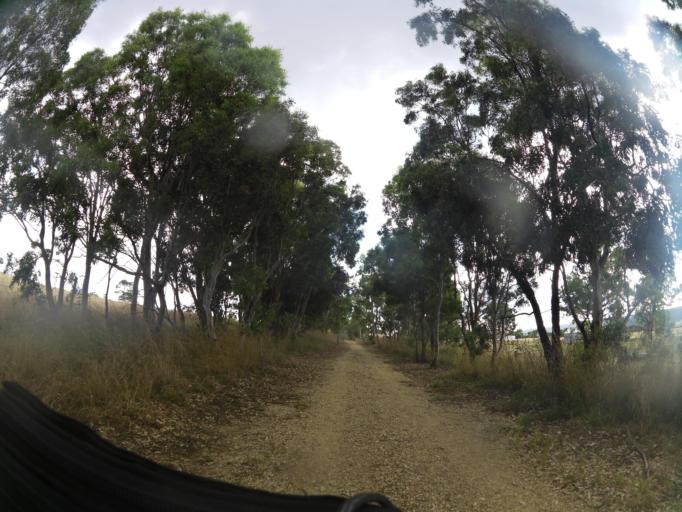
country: AU
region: Victoria
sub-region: Wellington
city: Heyfield
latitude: -38.0235
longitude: 146.6742
